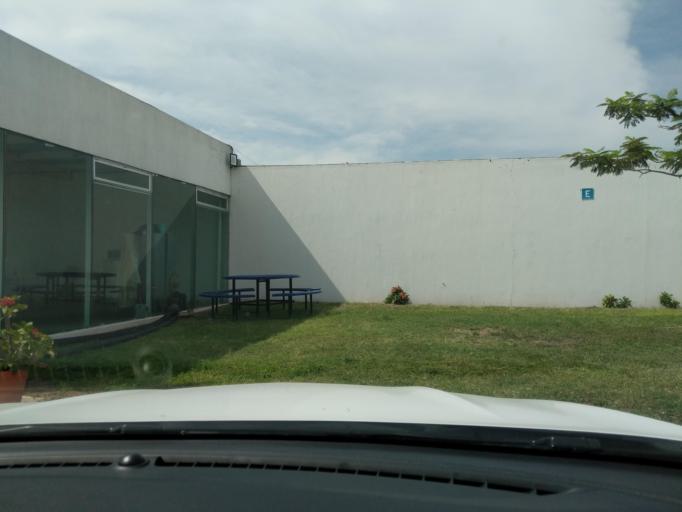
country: MX
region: Jalisco
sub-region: El Salto
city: Hacienda Vieja del Castillo (Castillo Viejo)
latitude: 20.5292
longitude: -103.2418
